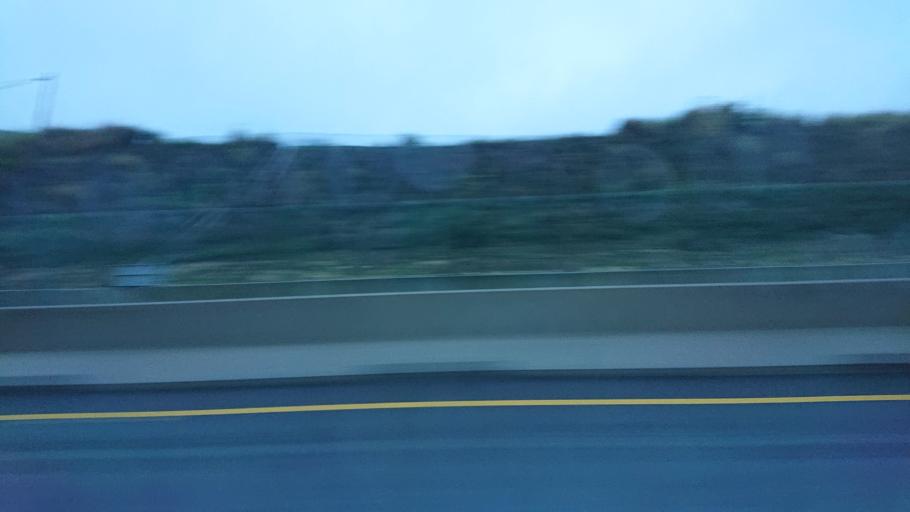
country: TW
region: Taiwan
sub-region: Miaoli
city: Miaoli
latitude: 24.5613
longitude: 120.7147
